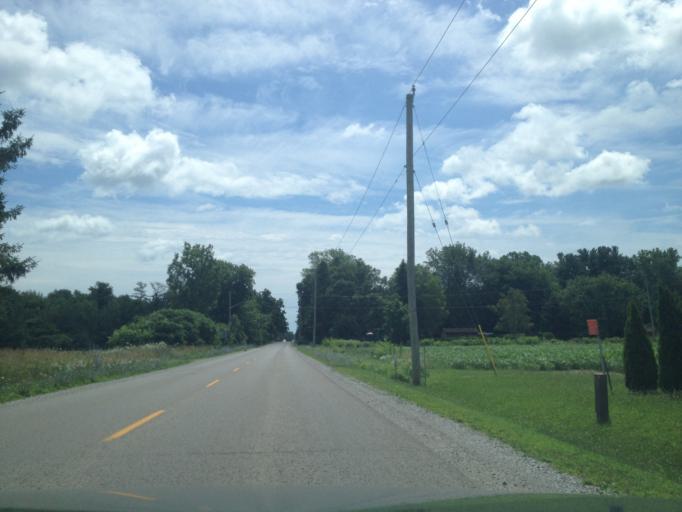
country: CA
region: Ontario
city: Norfolk County
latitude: 42.8088
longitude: -80.3193
